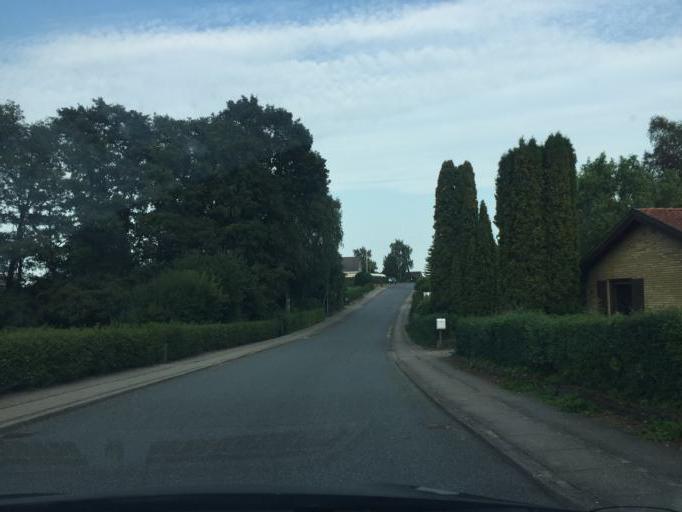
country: DK
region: South Denmark
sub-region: Kerteminde Kommune
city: Langeskov
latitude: 55.3105
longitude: 10.5851
